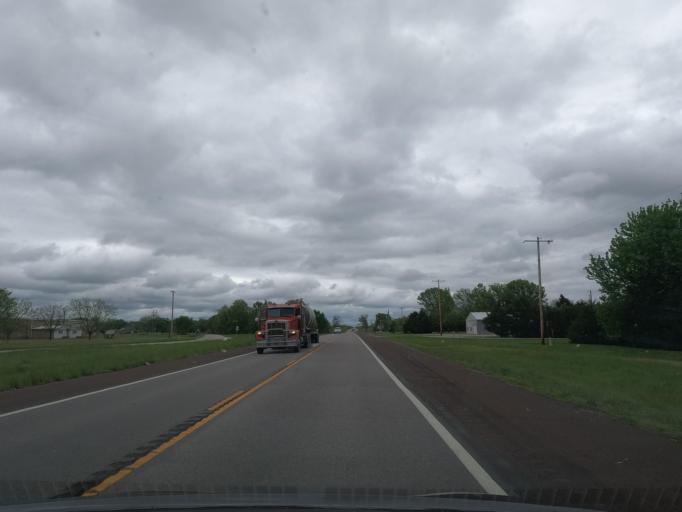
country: US
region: Kansas
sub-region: Labette County
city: Parsons
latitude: 37.3402
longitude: -95.0912
